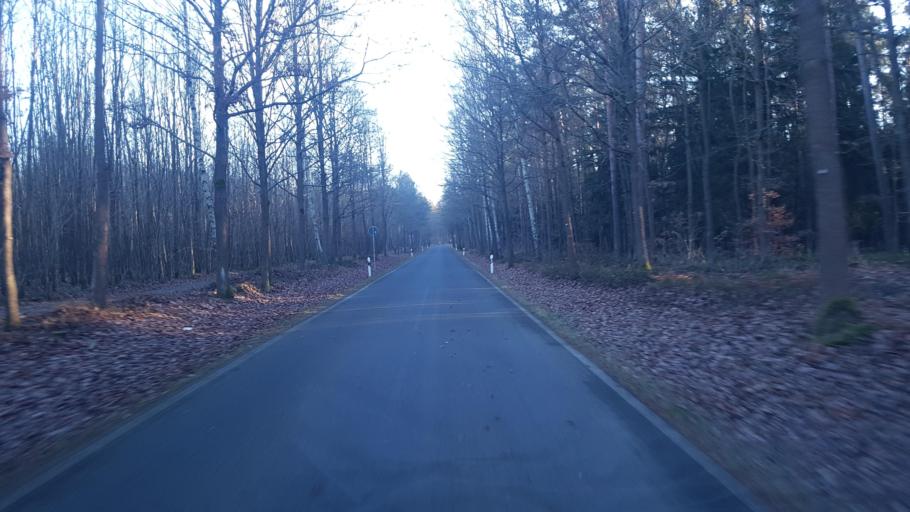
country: DE
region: Brandenburg
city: Tauer
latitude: 51.9312
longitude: 14.4835
